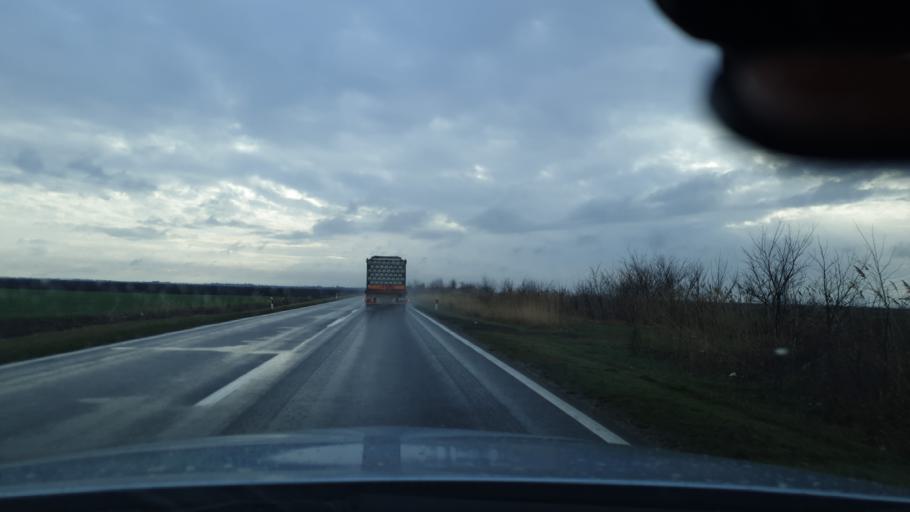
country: RS
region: Autonomna Pokrajina Vojvodina
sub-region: Juznobanatski Okrug
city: Kovin
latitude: 44.7897
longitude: 20.9180
